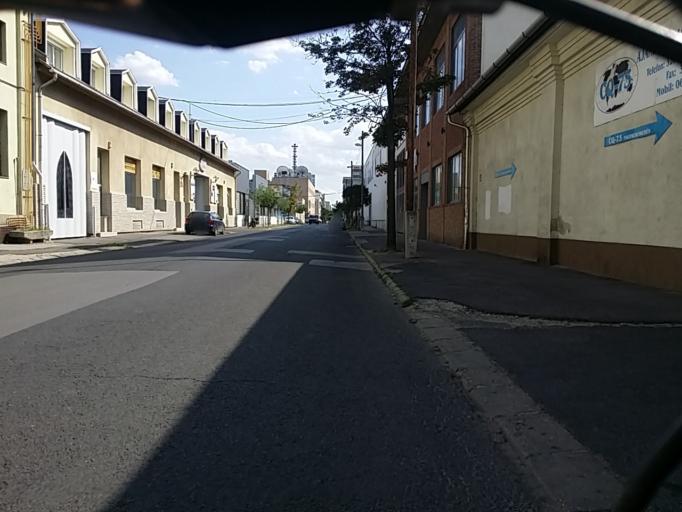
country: HU
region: Budapest
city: Budapest XIII. keruelet
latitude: 47.5390
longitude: 19.0716
